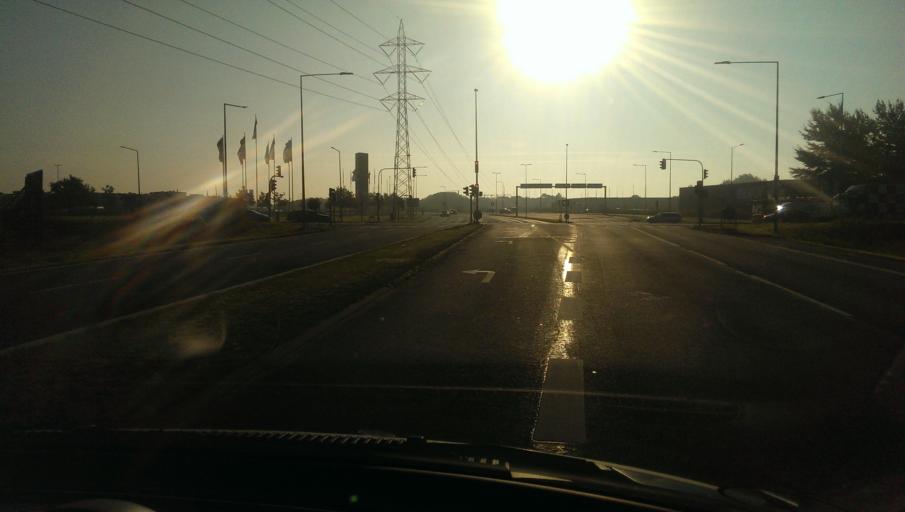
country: DK
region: South Denmark
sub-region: Kolding Kommune
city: Kolding
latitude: 55.5111
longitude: 9.4545
